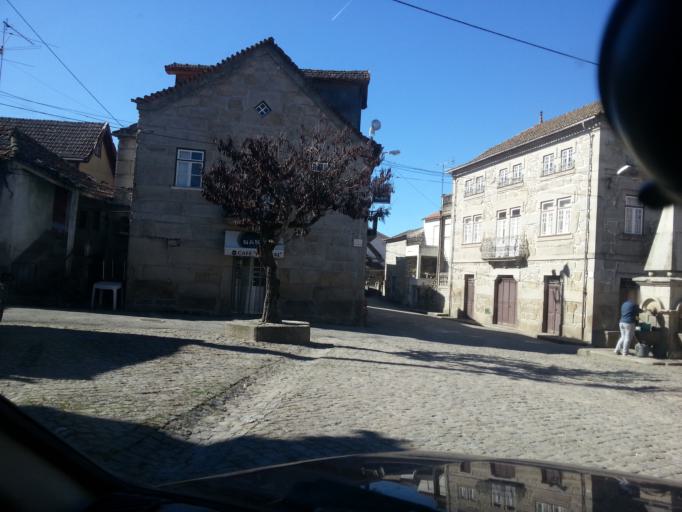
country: PT
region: Guarda
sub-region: Fornos de Algodres
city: Fornos de Algodres
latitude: 40.6093
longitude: -7.5074
